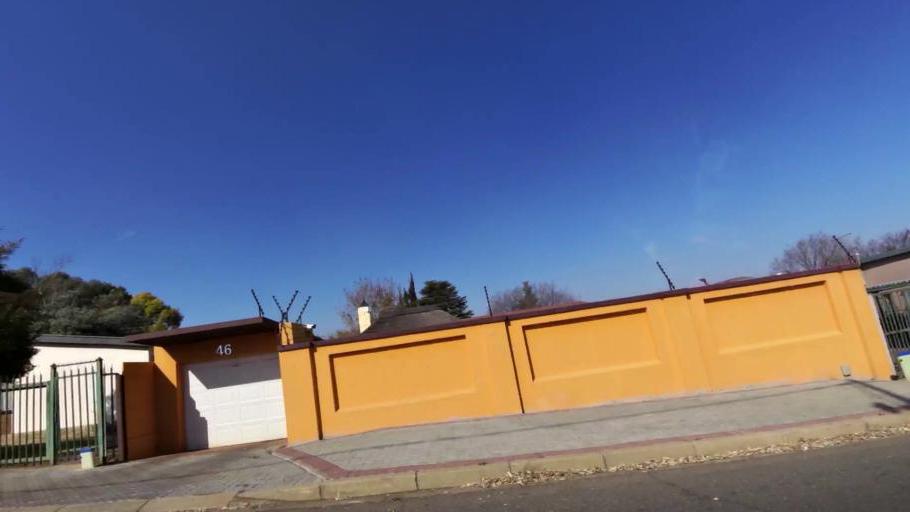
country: ZA
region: Gauteng
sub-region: City of Johannesburg Metropolitan Municipality
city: Johannesburg
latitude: -26.1769
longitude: 27.9831
